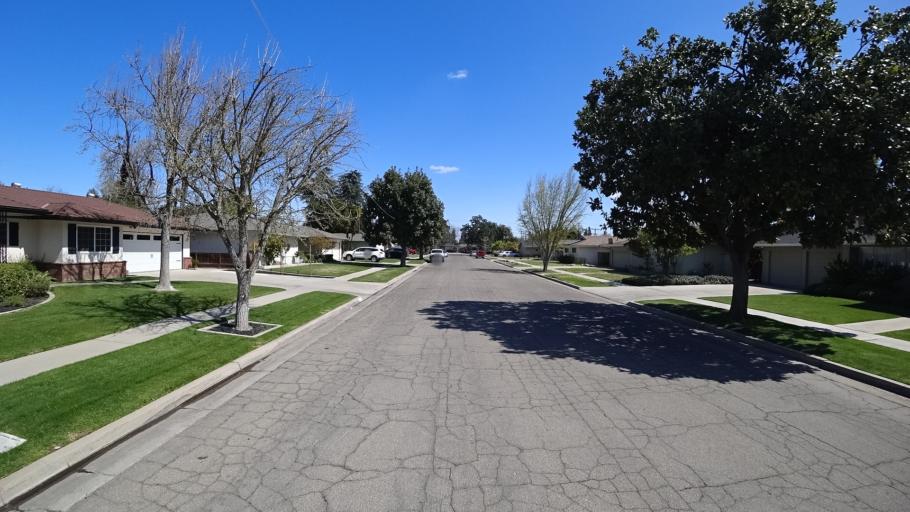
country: US
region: California
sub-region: Fresno County
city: Fresno
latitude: 36.8050
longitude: -119.8189
